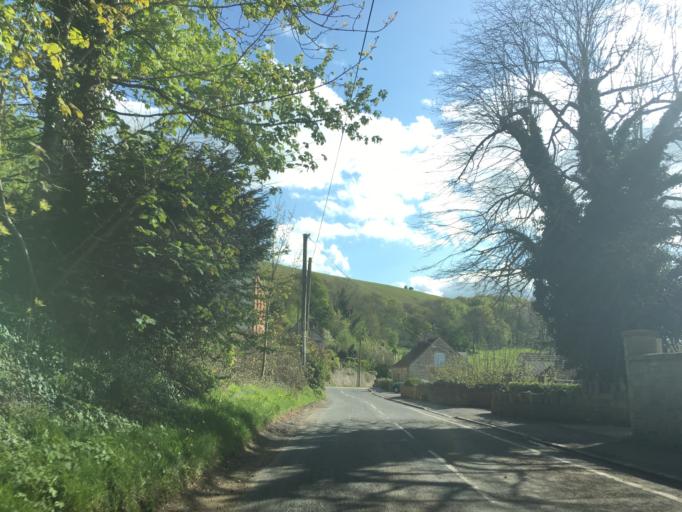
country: GB
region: England
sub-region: Gloucestershire
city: Stonehouse
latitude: 51.7313
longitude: -2.2490
